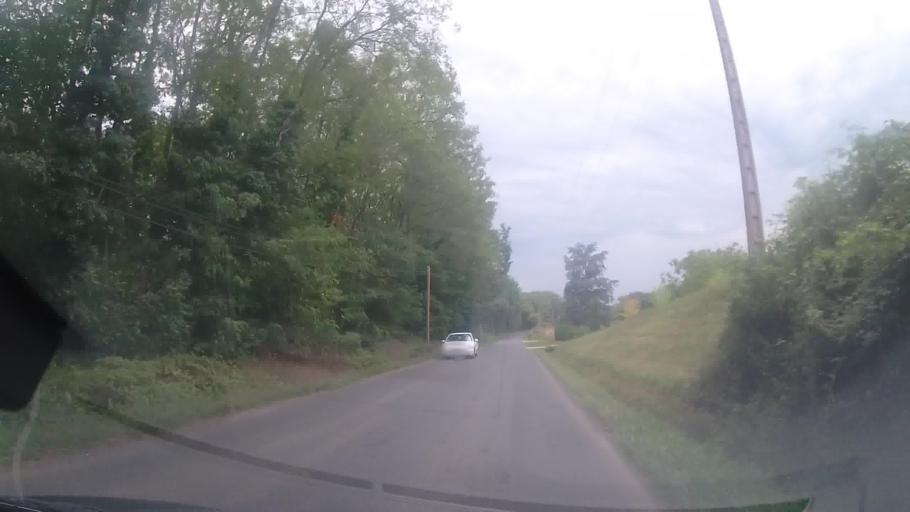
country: FR
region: Aquitaine
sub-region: Departement de la Dordogne
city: Carsac-Aillac
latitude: 44.8391
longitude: 1.3000
